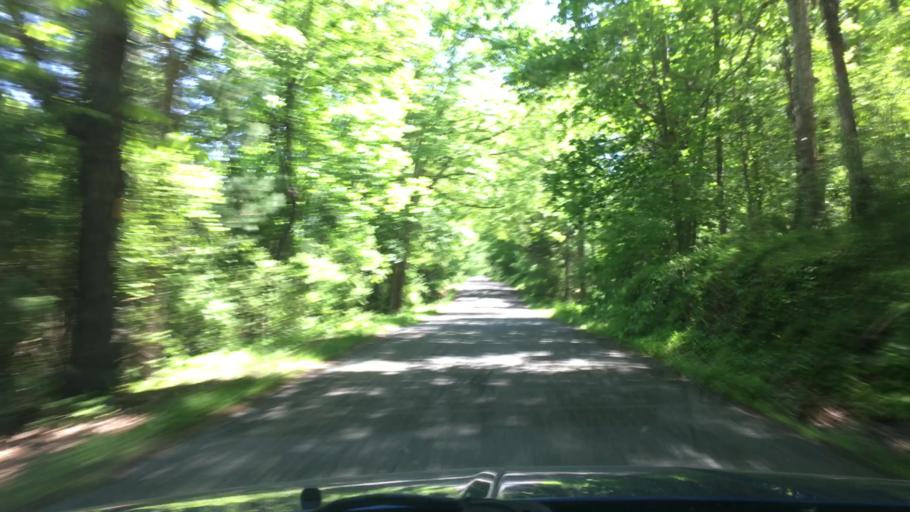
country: US
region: Virginia
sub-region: Bath County
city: Warm Springs
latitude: 38.0756
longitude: -79.5880
